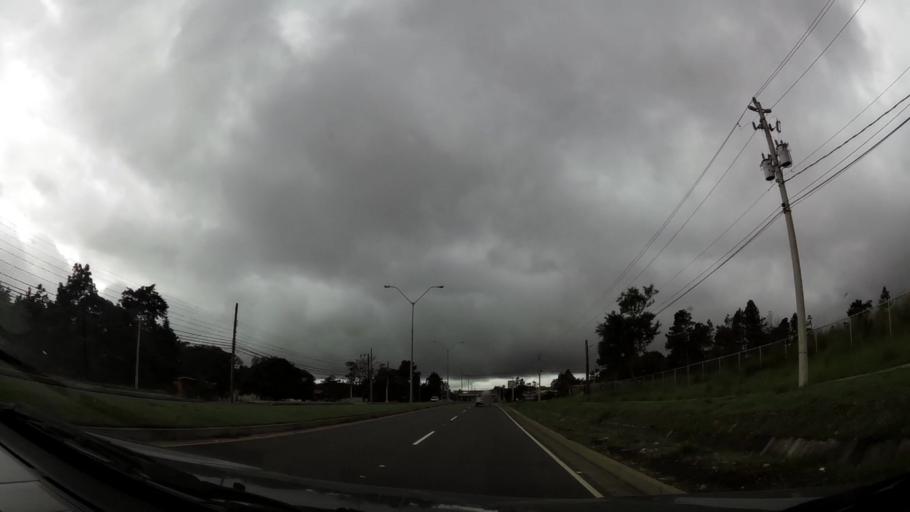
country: PA
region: Chiriqui
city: Palmira
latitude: 8.7417
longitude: -82.4330
